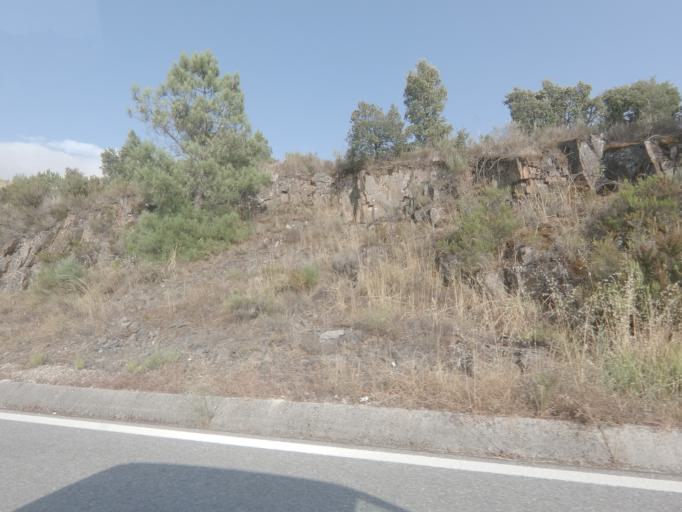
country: PT
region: Viseu
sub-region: Tabuaco
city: Tabuaco
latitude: 41.1434
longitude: -7.5450
